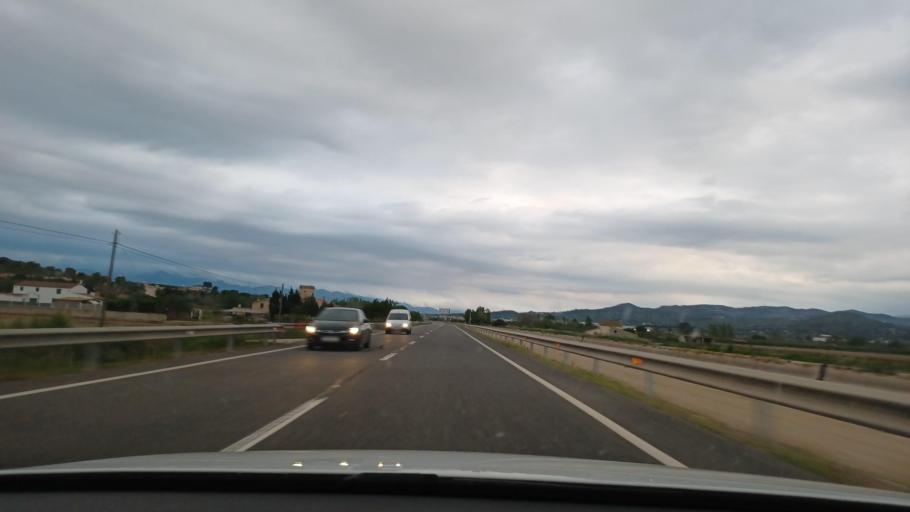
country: ES
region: Catalonia
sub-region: Provincia de Tarragona
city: Amposta
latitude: 40.7375
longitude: 0.5666
